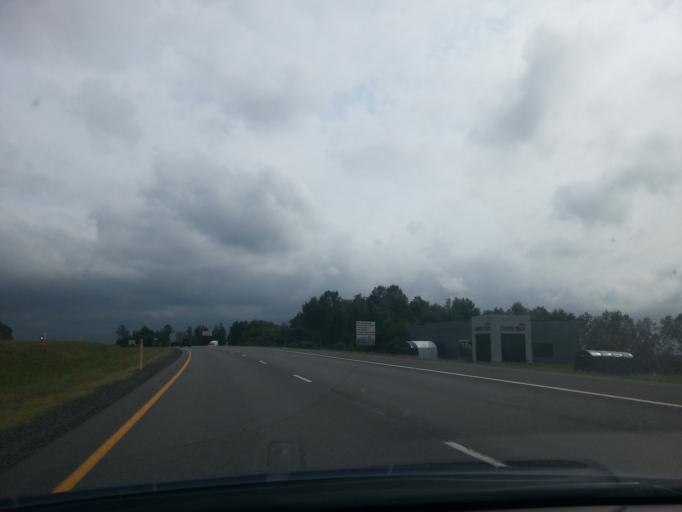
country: US
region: Maine
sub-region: Aroostook County
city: Houlton
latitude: 46.1327
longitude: -67.6099
